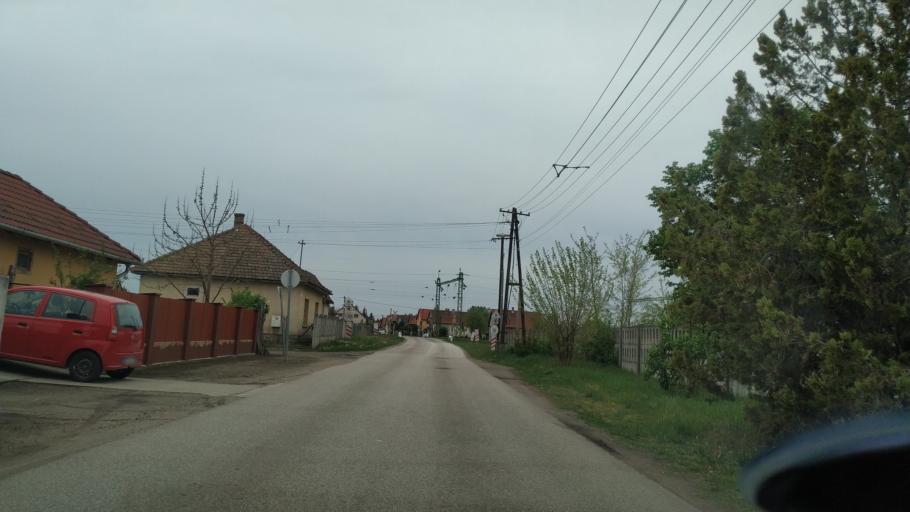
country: HU
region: Pest
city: Nagykata
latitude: 47.4154
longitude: 19.7281
